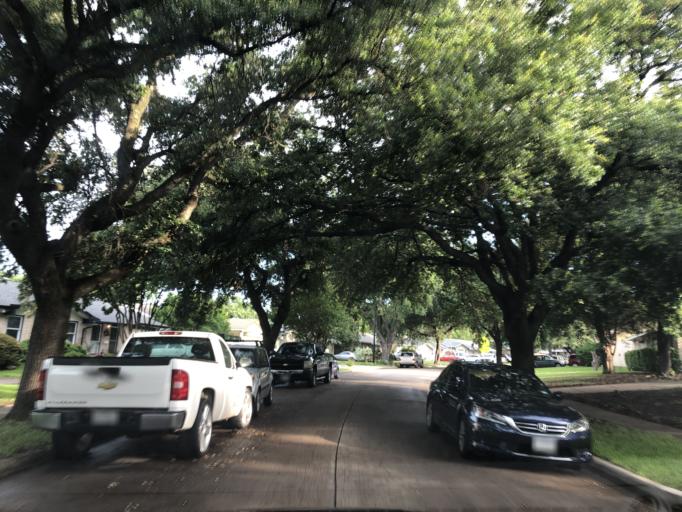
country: US
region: Texas
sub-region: Dallas County
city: Sunnyvale
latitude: 32.8480
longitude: -96.6018
